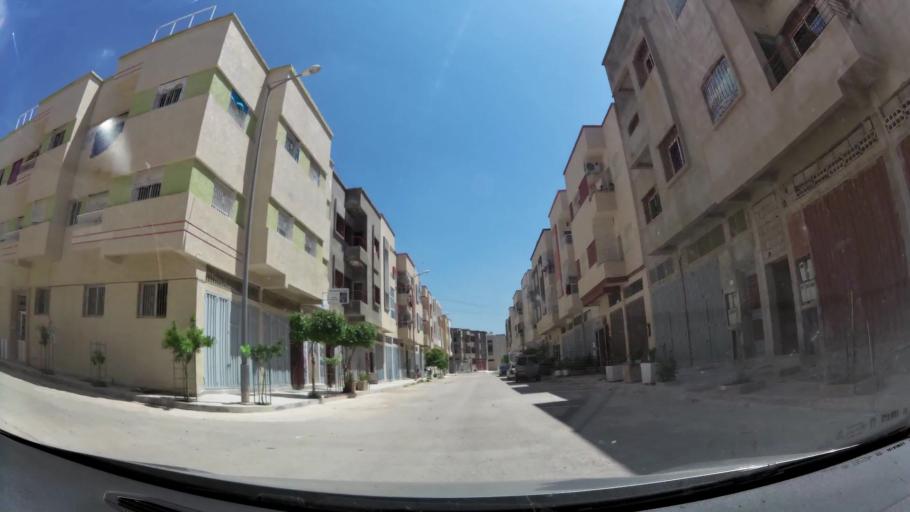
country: MA
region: Fes-Boulemane
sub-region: Fes
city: Fes
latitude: 34.0213
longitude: -5.0576
